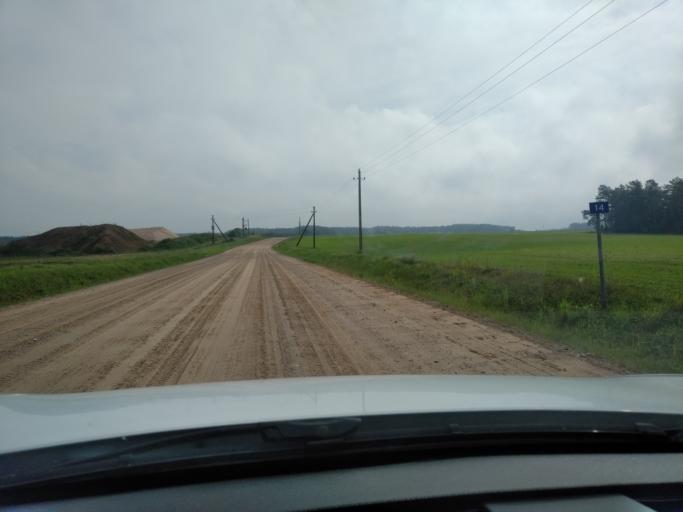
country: LT
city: Svencionys
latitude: 55.2451
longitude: 26.1608
